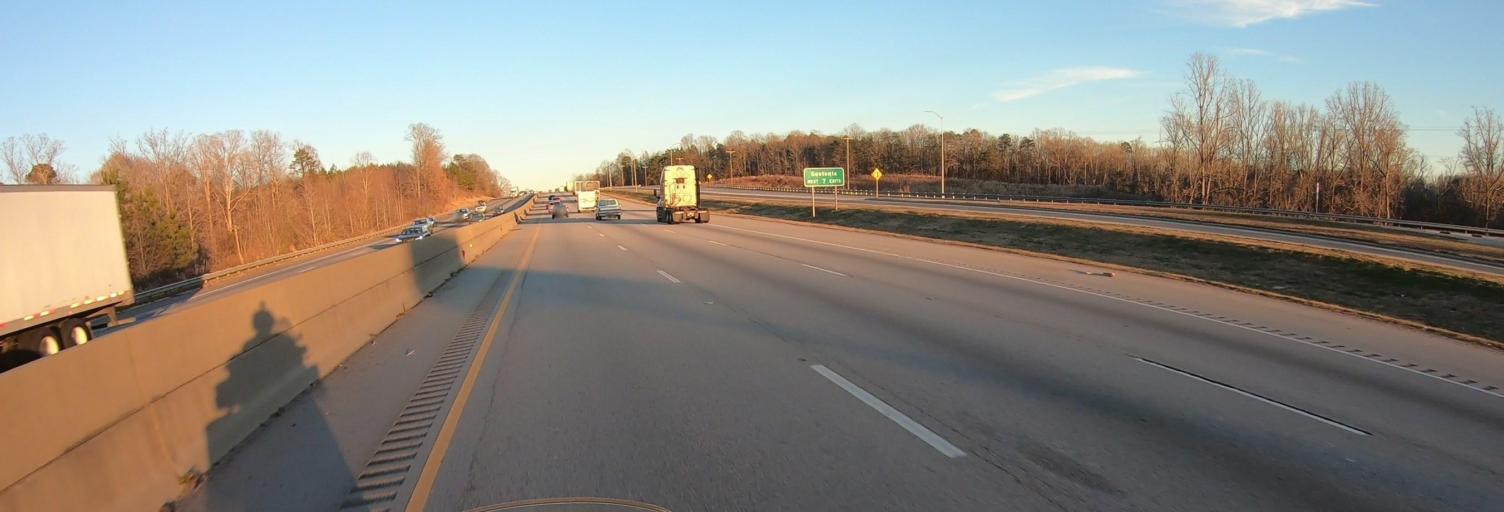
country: US
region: North Carolina
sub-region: Gaston County
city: Bessemer City
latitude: 35.2593
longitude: -81.2774
